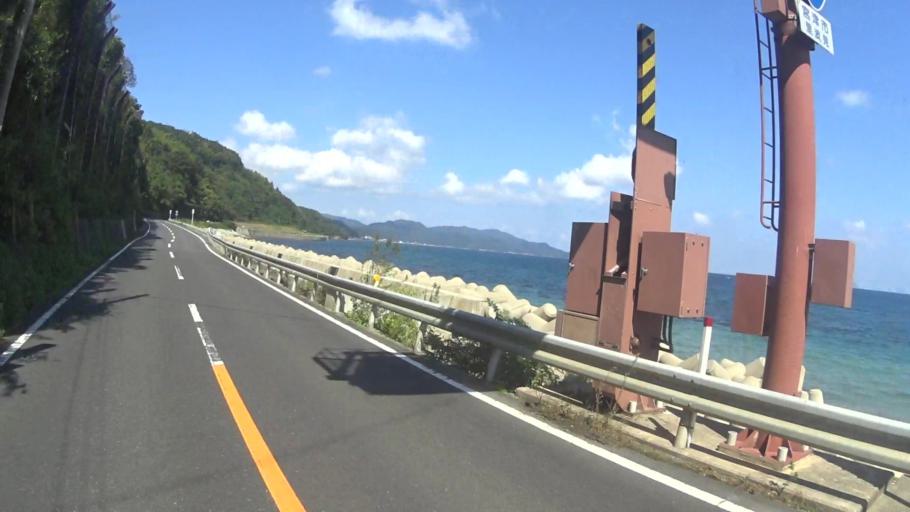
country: JP
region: Kyoto
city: Miyazu
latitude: 35.6274
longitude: 135.2456
